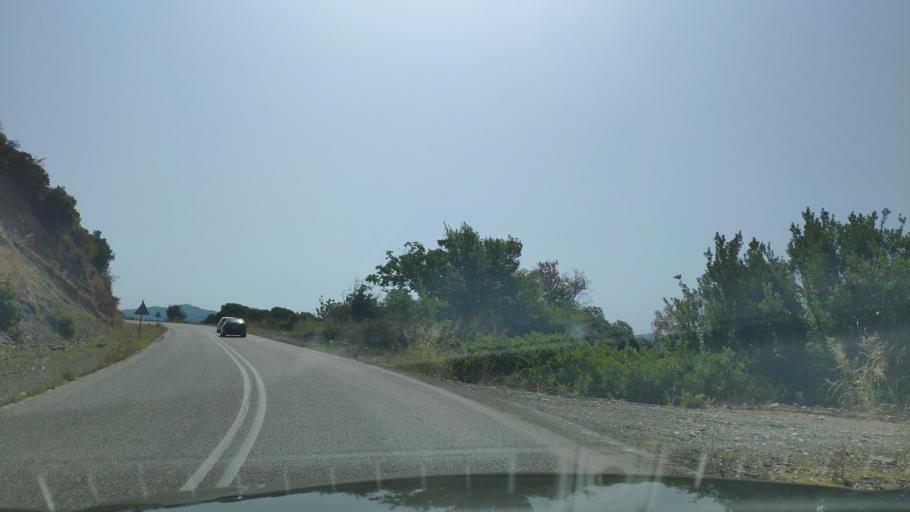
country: GR
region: Epirus
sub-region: Nomos Artas
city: Peta
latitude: 39.1682
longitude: 21.0646
